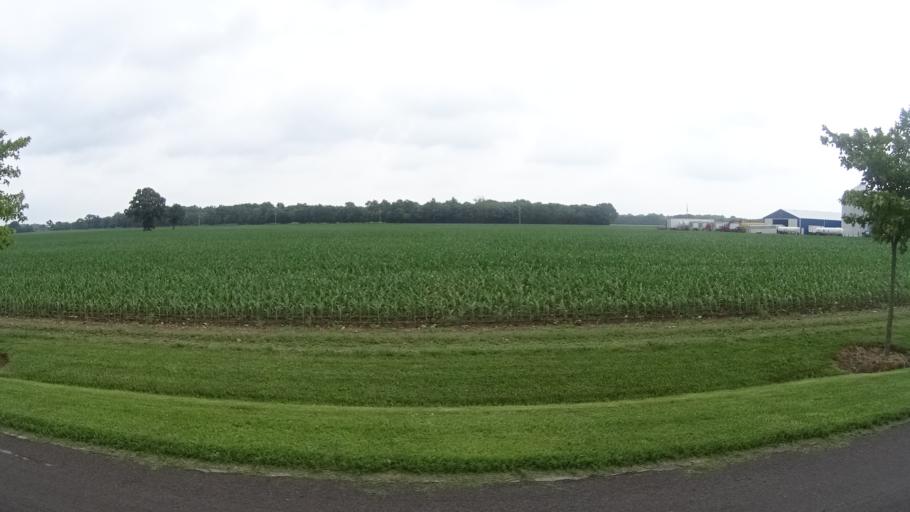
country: US
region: Ohio
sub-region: Huron County
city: Bellevue
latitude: 41.3532
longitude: -82.7856
